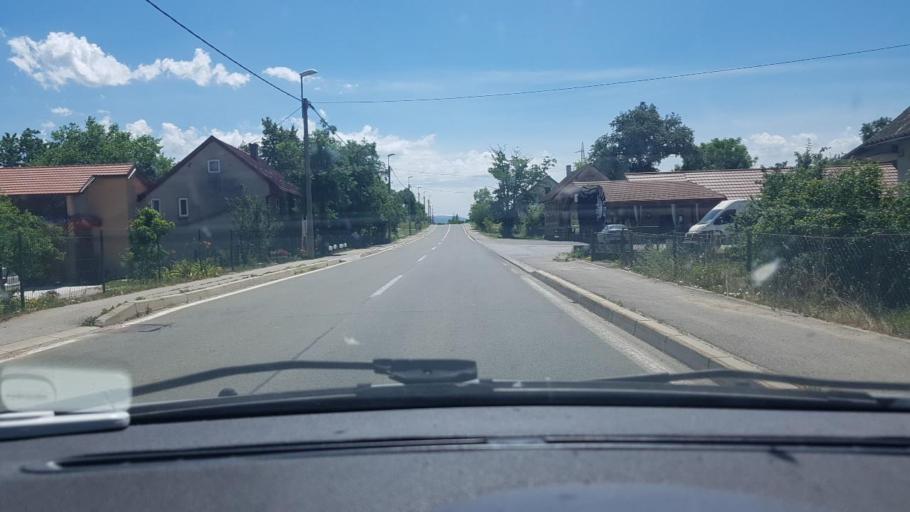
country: HR
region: Licko-Senjska
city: Otocac
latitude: 44.8651
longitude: 15.2582
